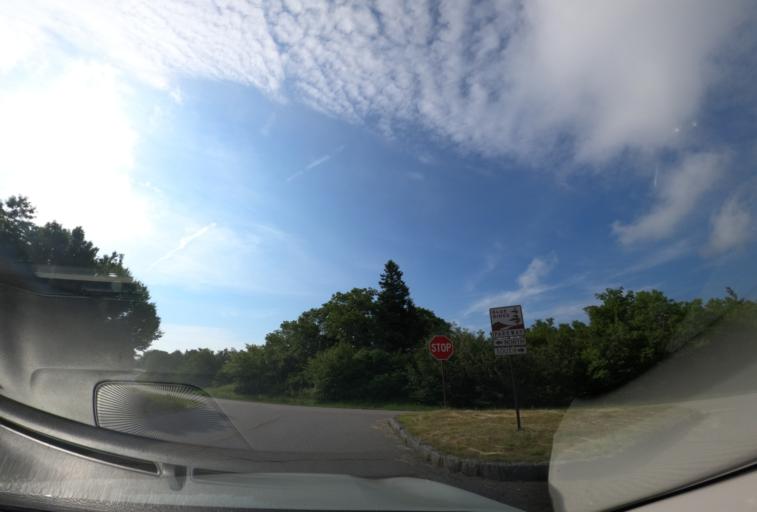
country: US
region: North Carolina
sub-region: Transylvania County
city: Brevard
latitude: 35.2987
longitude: -82.9112
